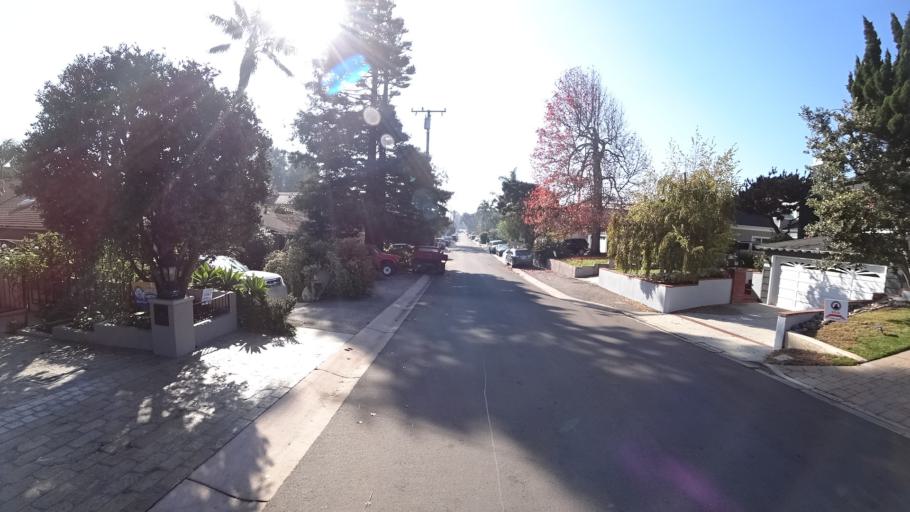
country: US
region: California
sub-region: Los Angeles County
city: Manhattan Beach
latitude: 33.8910
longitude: -118.3987
